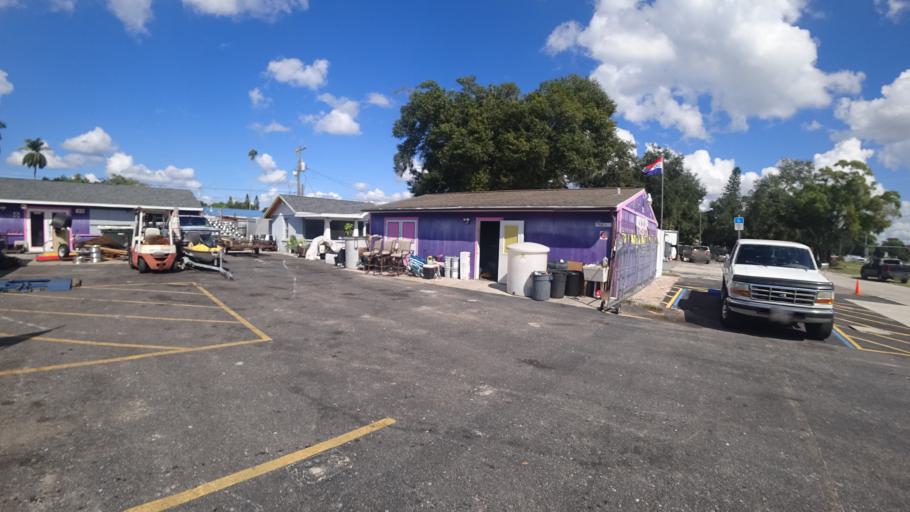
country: US
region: Florida
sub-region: Manatee County
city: South Bradenton
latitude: 27.4740
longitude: -82.5730
